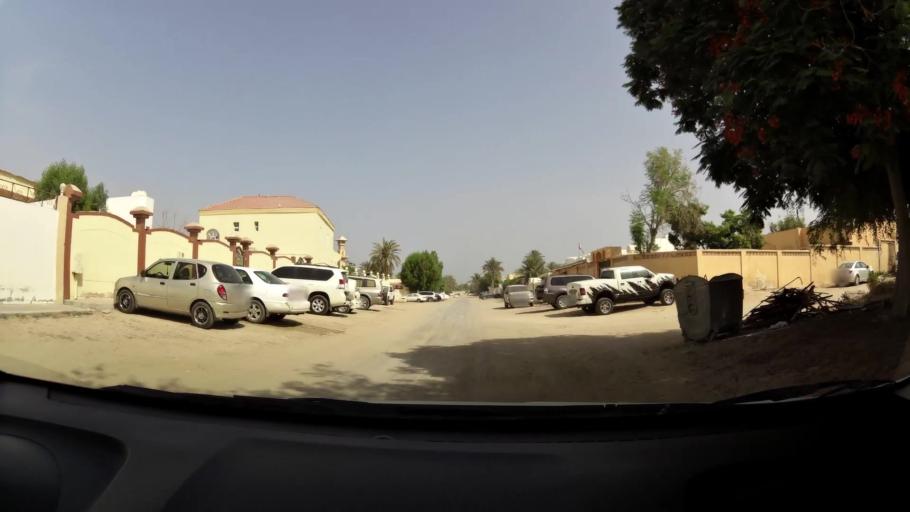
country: AE
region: Ash Shariqah
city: Sharjah
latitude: 25.3459
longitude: 55.4176
